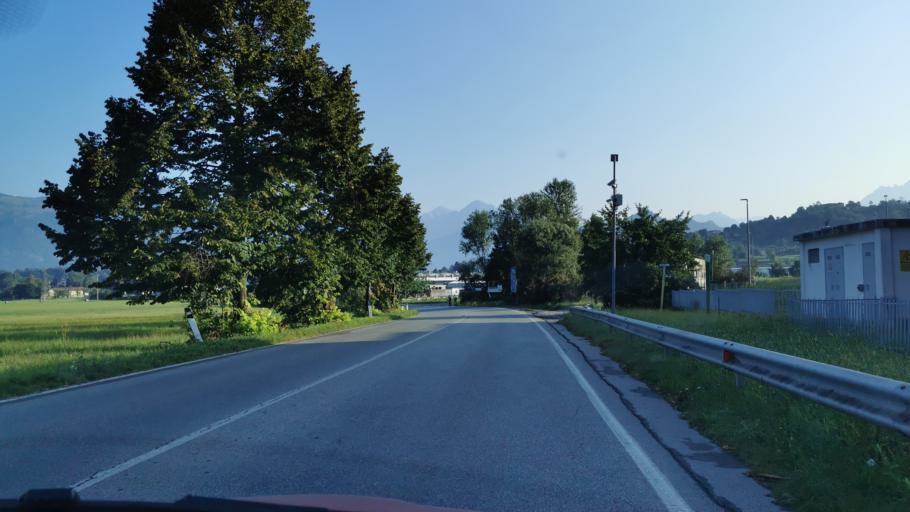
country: IT
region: Lombardy
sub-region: Provincia di Lecco
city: Dolzago
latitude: 45.7750
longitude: 9.3397
